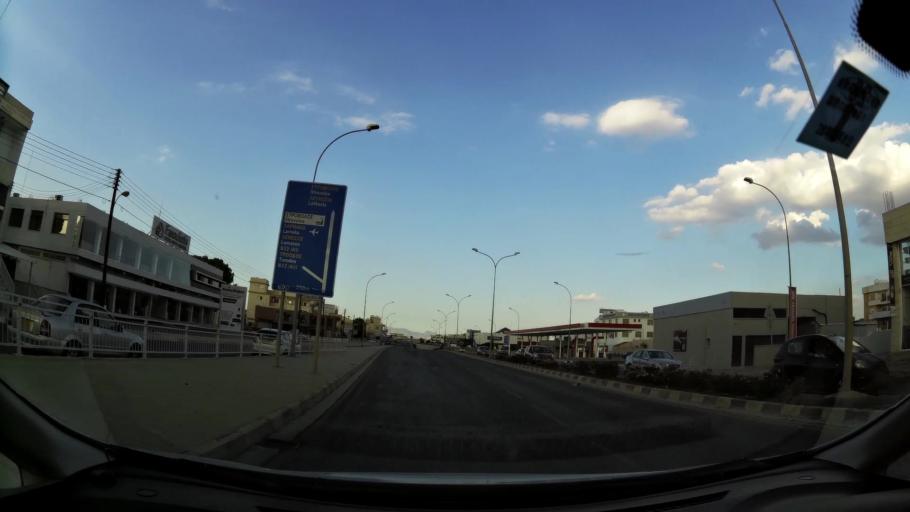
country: CY
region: Lefkosia
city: Tseri
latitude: 35.1231
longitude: 33.3210
